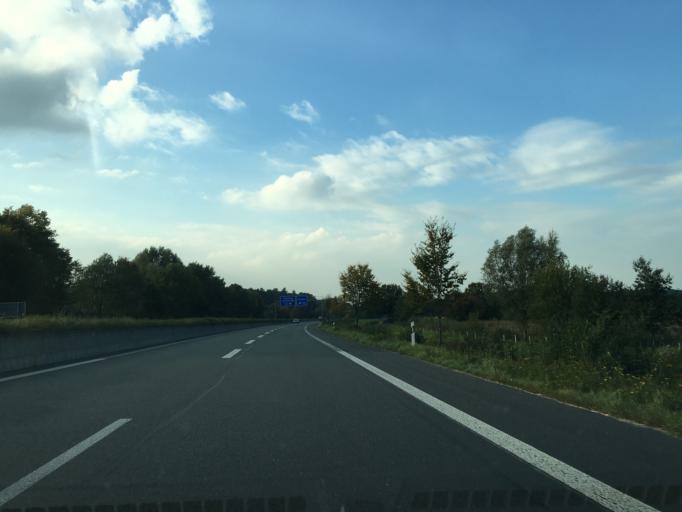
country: DE
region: North Rhine-Westphalia
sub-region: Regierungsbezirk Munster
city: Dulmen
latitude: 51.8460
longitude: 7.2936
